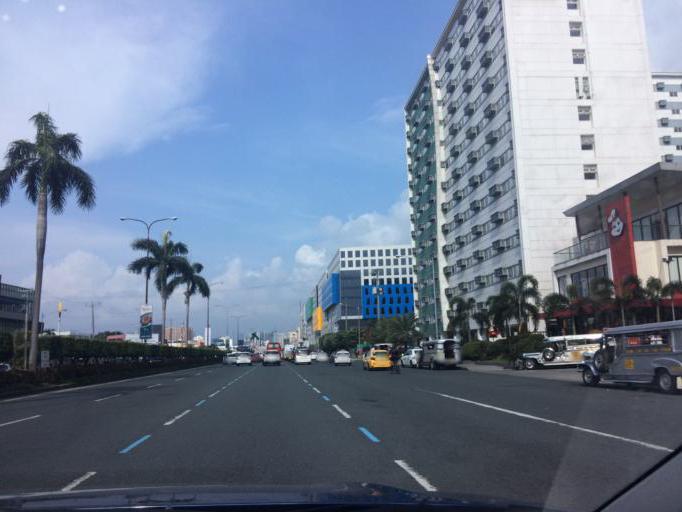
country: PH
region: Metro Manila
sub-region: Makati City
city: Makati City
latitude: 14.5357
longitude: 120.9871
